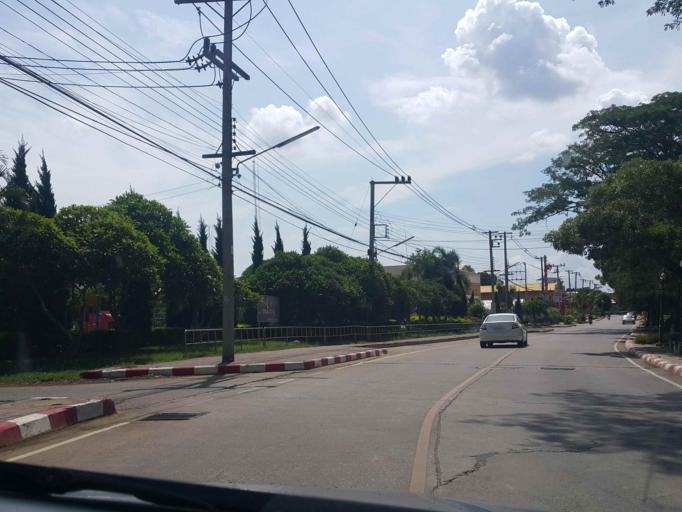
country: TH
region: Phayao
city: Phayao
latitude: 19.1660
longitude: 99.9051
